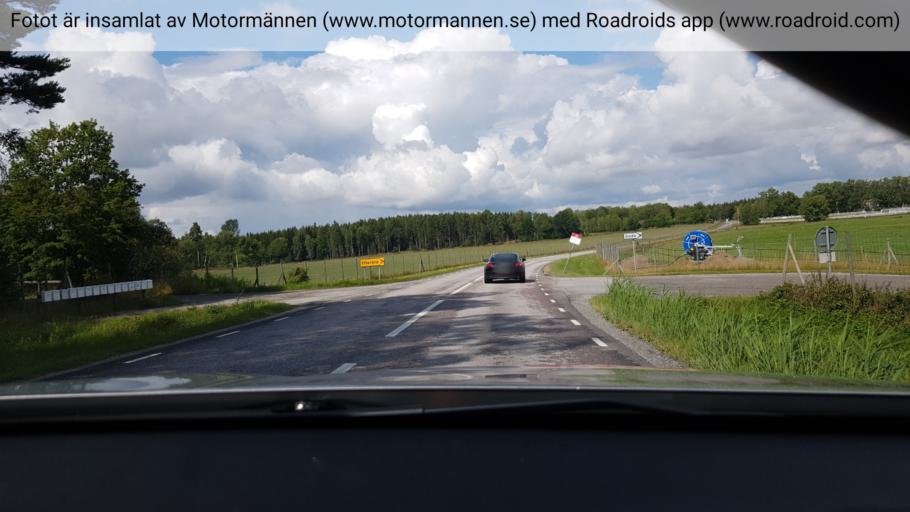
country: SE
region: Stockholm
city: Stenhamra
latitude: 59.3205
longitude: 17.6322
